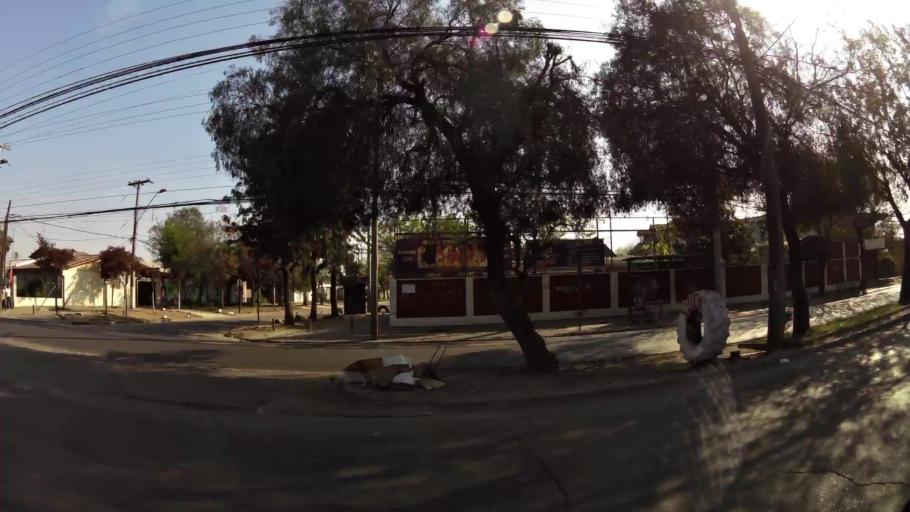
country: CL
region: Santiago Metropolitan
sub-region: Provincia de Santiago
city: Lo Prado
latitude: -33.3830
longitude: -70.6818
